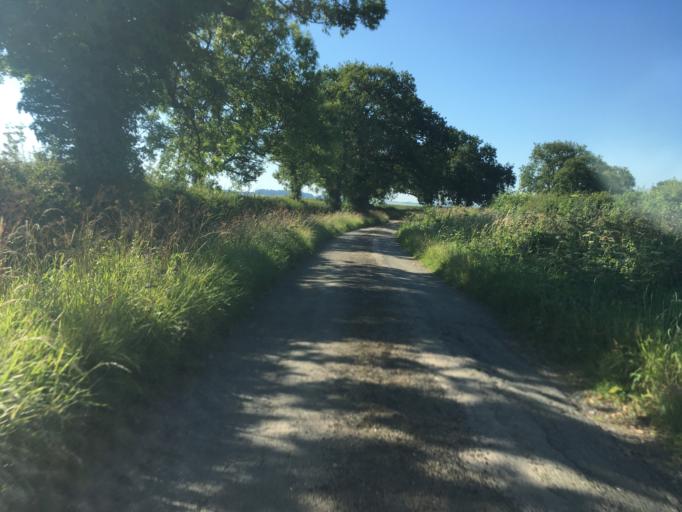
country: GB
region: England
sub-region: South Gloucestershire
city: Chipping Sodbury
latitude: 51.5162
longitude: -2.4002
